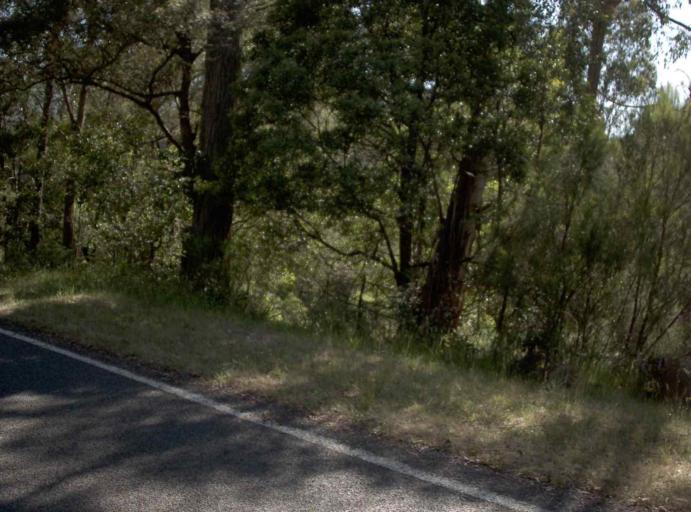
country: AU
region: New South Wales
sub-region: Bombala
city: Bombala
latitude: -37.3428
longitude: 148.6992
